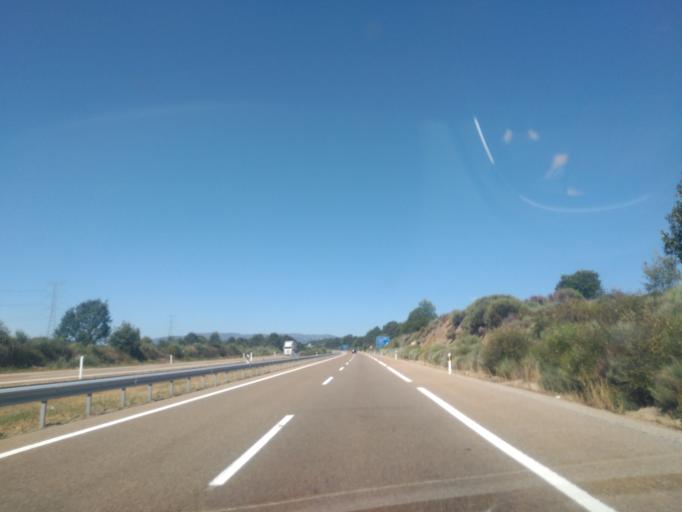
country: ES
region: Castille and Leon
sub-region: Provincia de Zamora
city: Palacios de Sanabria
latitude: 42.0497
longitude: -6.5334
